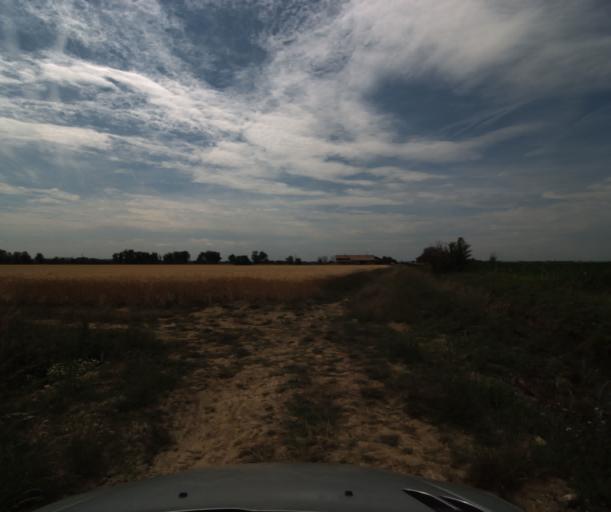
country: FR
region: Midi-Pyrenees
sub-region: Departement de la Haute-Garonne
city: Lacasse
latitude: 43.4149
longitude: 1.2624
